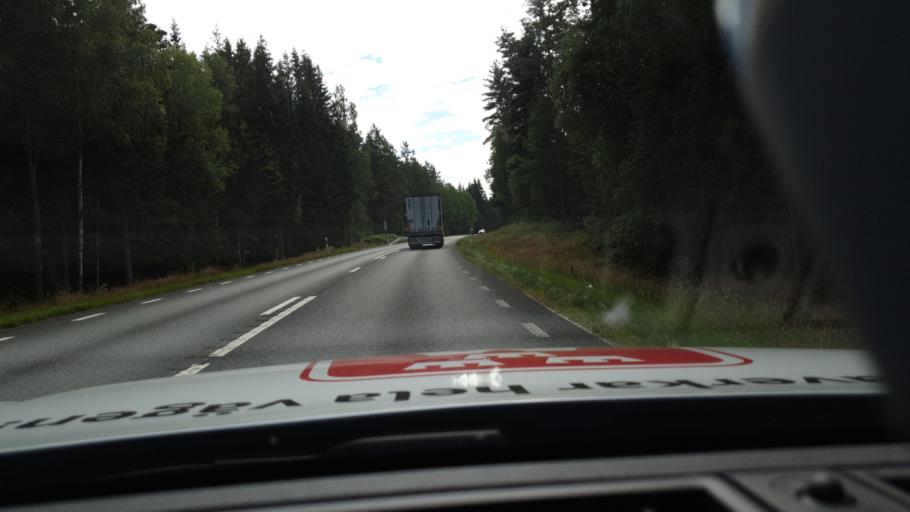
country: SE
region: Joenkoeping
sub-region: Savsjo Kommun
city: Vrigstad
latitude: 57.3855
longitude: 14.3967
